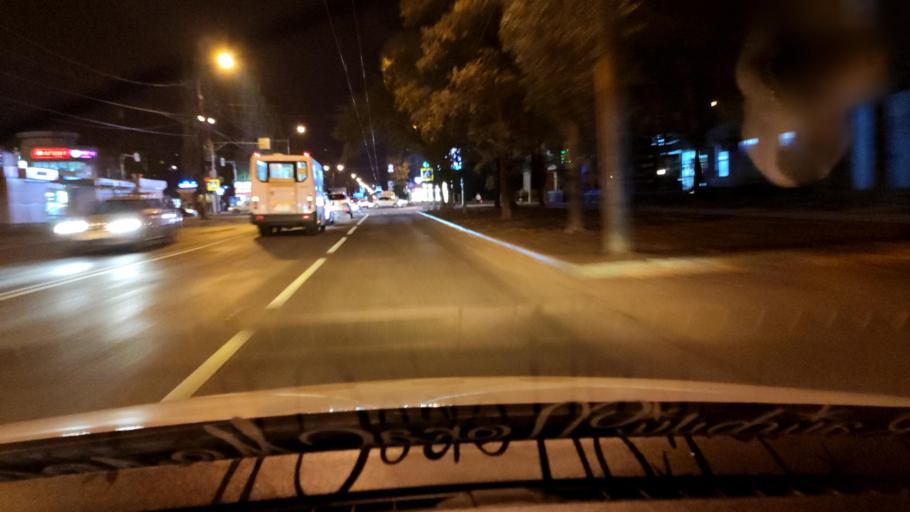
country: RU
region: Voronezj
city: Voronezh
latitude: 51.7058
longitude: 39.1744
